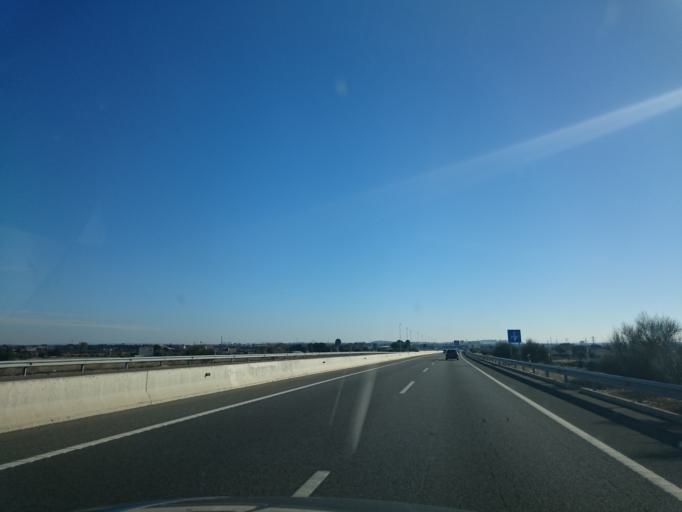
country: ES
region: Catalonia
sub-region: Provincia de Tarragona
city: Cambrils
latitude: 41.0846
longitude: 1.0626
